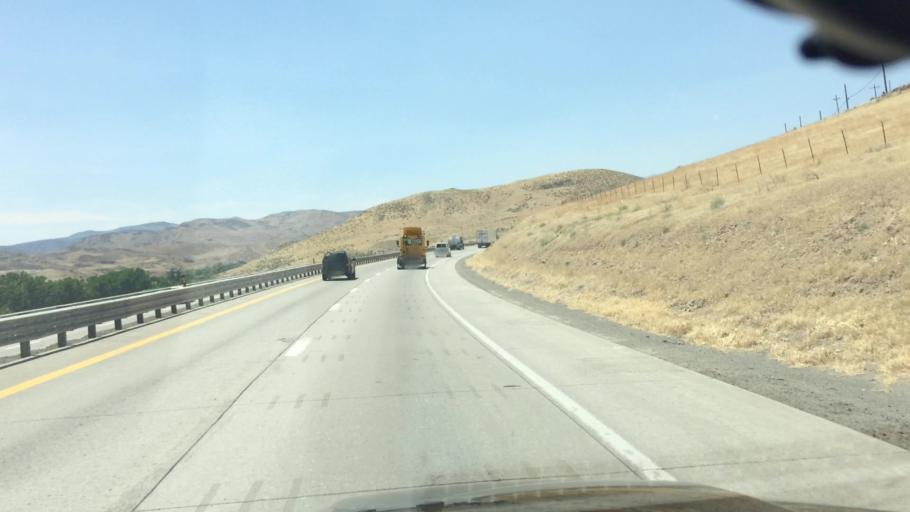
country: US
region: Nevada
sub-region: Washoe County
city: Sparks
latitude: 39.5333
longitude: -119.6057
